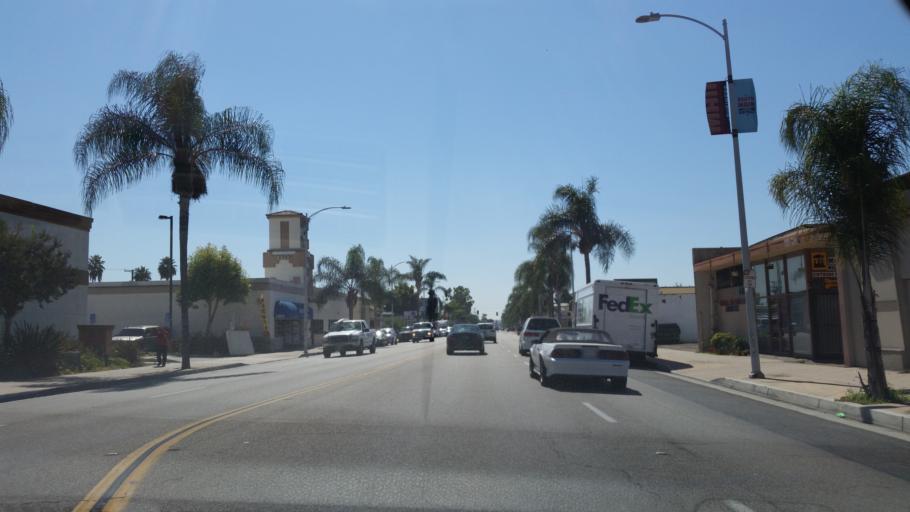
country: US
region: California
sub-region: Orange County
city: Santa Ana
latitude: 33.7221
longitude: -117.8680
